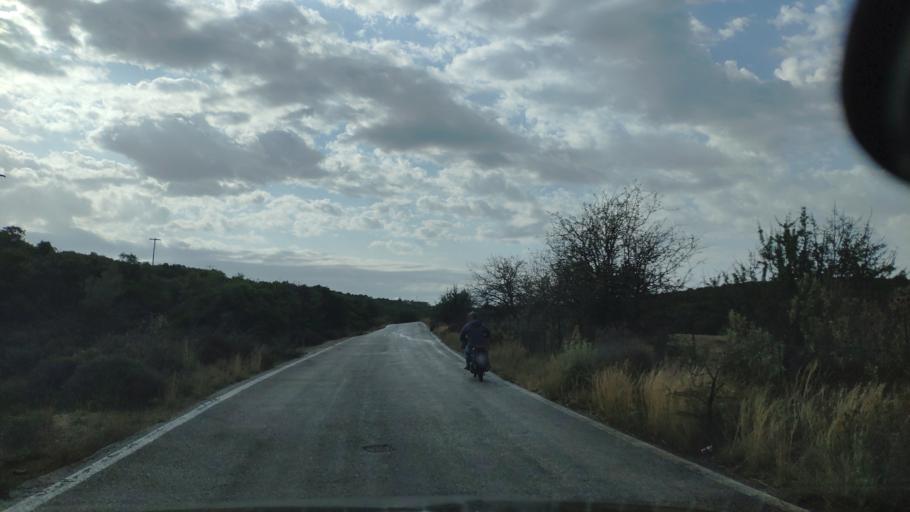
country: GR
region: West Greece
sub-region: Nomos Aitolias kai Akarnanias
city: Sardinia
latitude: 38.8833
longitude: 21.2450
